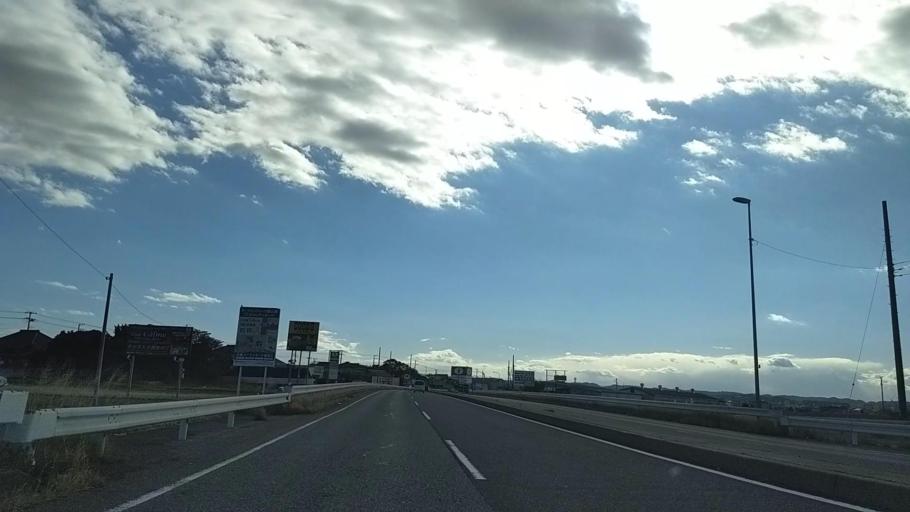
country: JP
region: Chiba
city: Tateyama
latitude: 35.0210
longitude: 139.8693
